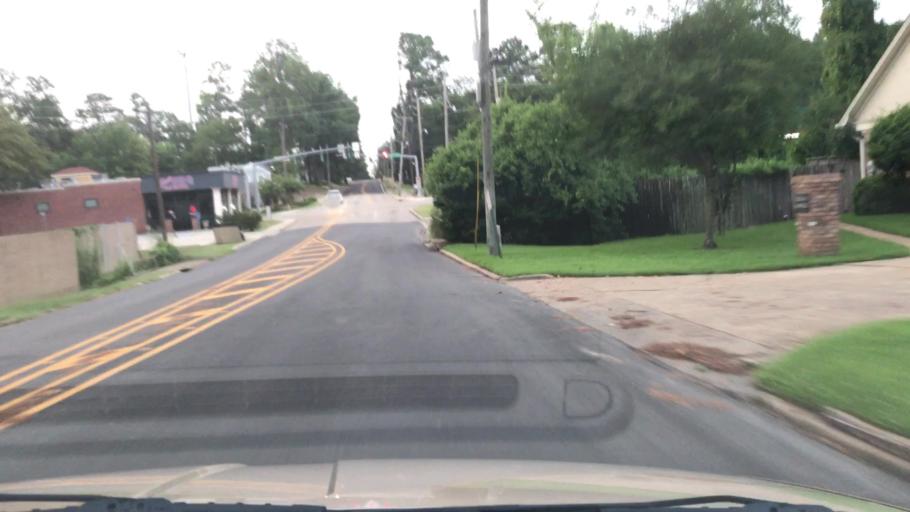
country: US
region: Louisiana
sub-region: Bossier Parish
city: Bossier City
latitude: 32.4556
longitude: -93.7503
